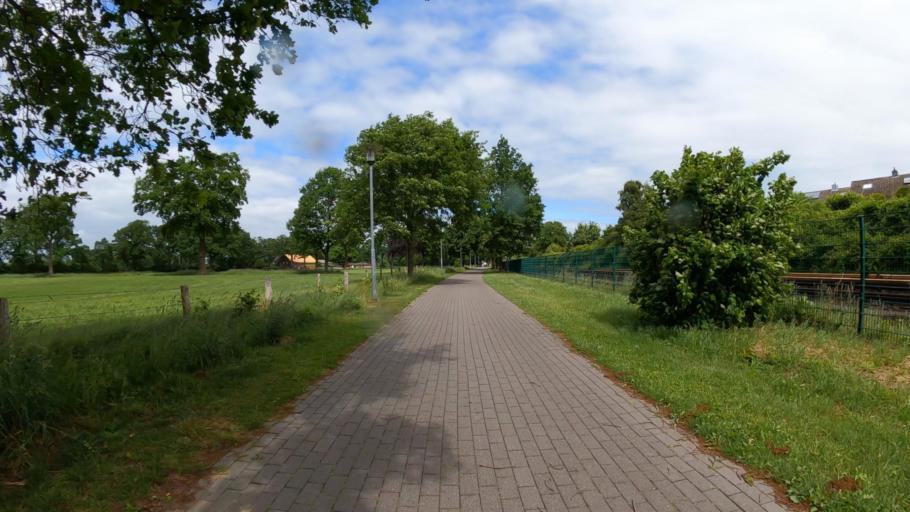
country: DE
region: Schleswig-Holstein
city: Norderstedt
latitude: 53.6929
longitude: 9.9865
